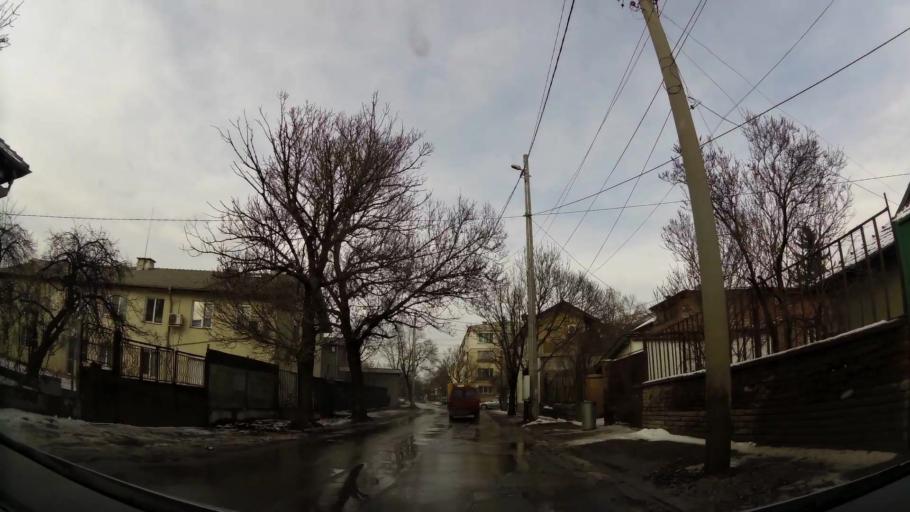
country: BG
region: Sofia-Capital
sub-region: Stolichna Obshtina
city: Sofia
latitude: 42.6957
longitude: 23.3751
